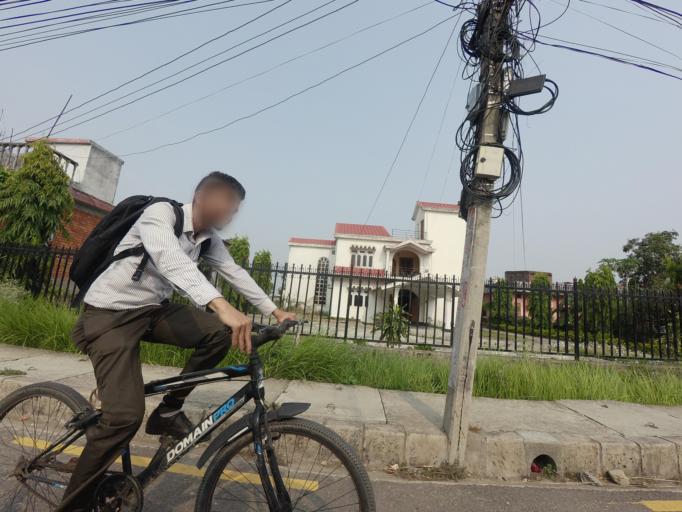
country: NP
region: Western Region
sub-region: Lumbini Zone
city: Bhairahawa
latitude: 27.5230
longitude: 83.4577
